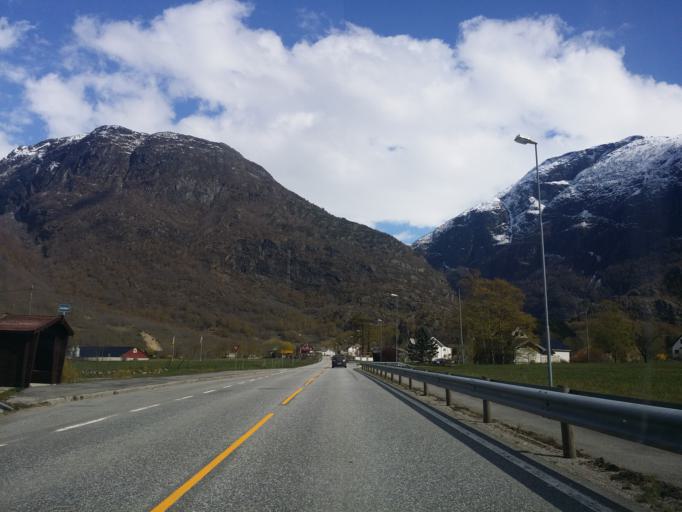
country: NO
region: Hordaland
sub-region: Eidfjord
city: Eidfjord
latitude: 60.4245
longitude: 7.1194
